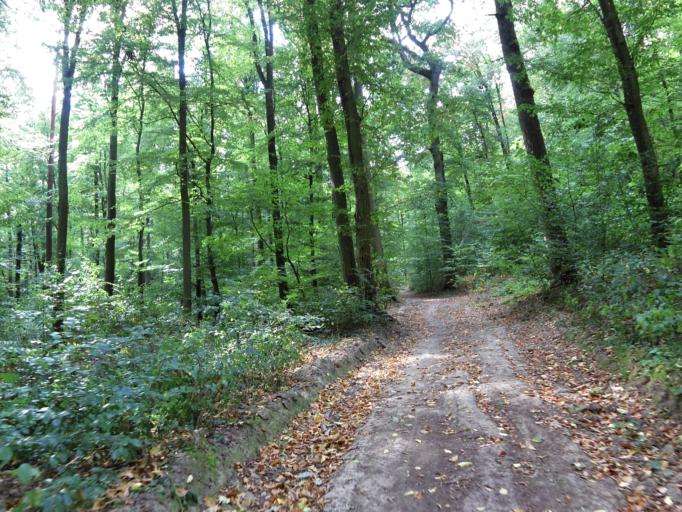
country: DE
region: Bavaria
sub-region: Regierungsbezirk Unterfranken
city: Hochberg
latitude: 49.7864
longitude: 9.8686
